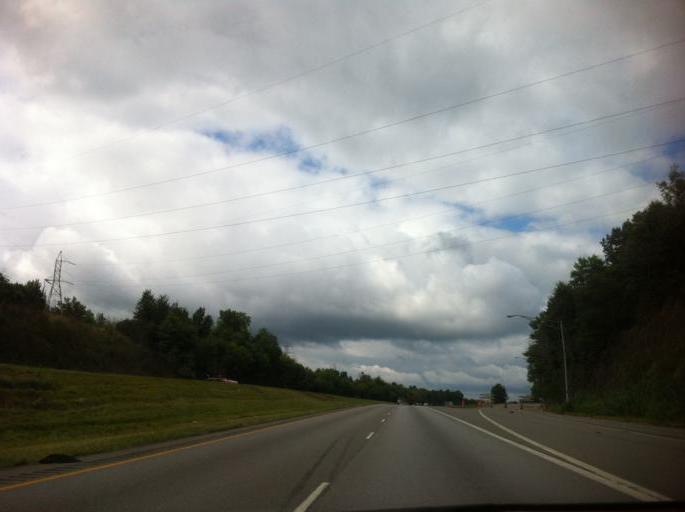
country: US
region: Ohio
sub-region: Trumbull County
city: Masury
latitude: 41.1804
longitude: -80.5288
